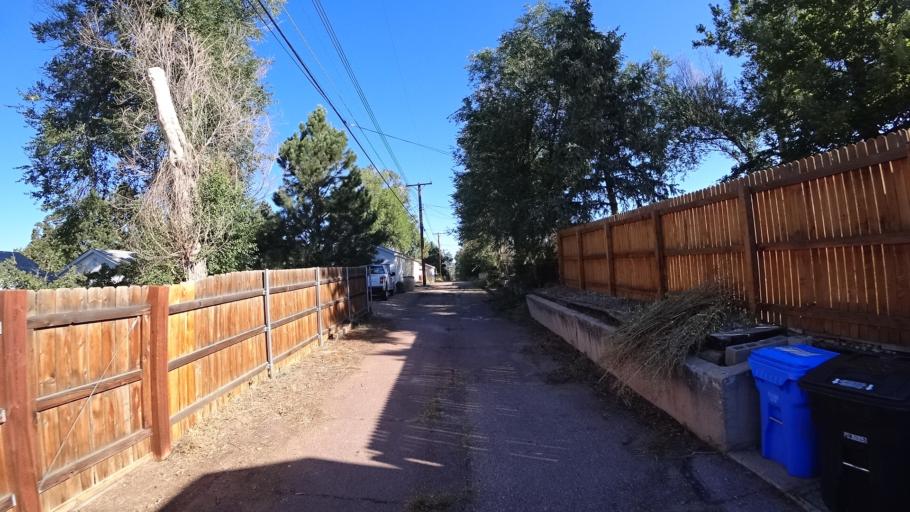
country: US
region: Colorado
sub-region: El Paso County
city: Colorado Springs
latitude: 38.8641
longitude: -104.7959
